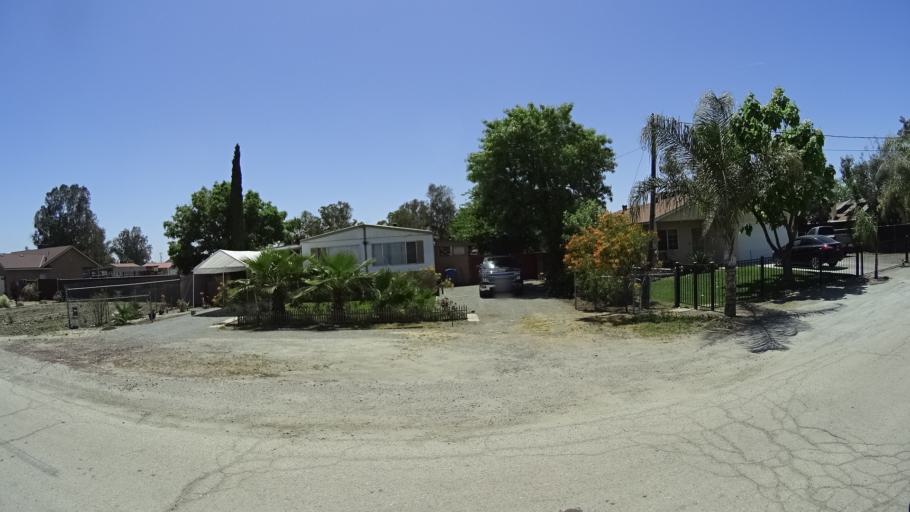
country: US
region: California
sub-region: Kings County
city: Corcoran
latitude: 36.1181
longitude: -119.5802
